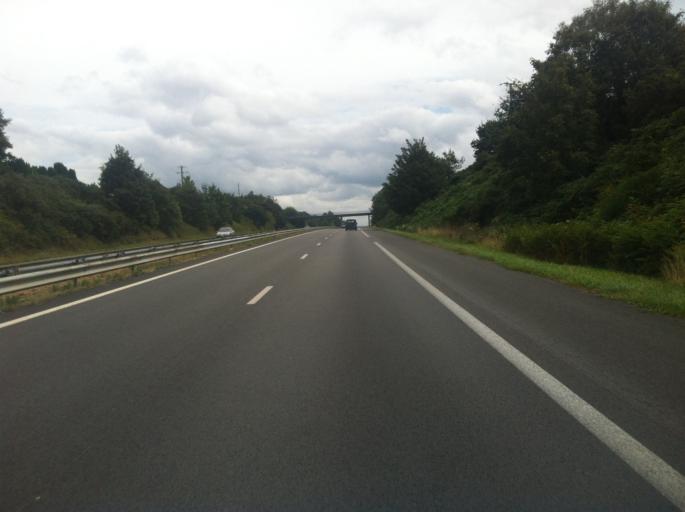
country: FR
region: Brittany
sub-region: Departement du Finistere
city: Guerlesquin
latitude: 48.5704
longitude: -3.6141
